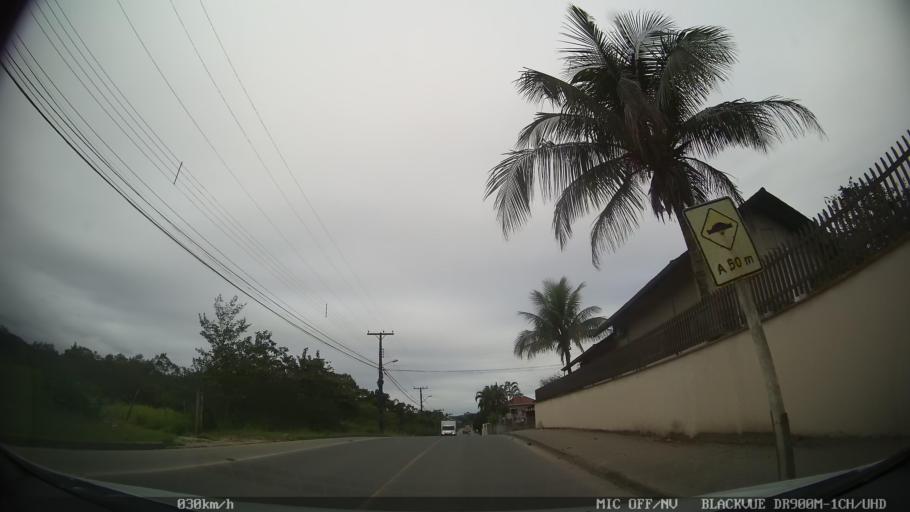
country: BR
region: Santa Catarina
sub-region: Joinville
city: Joinville
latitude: -26.3209
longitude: -48.9113
